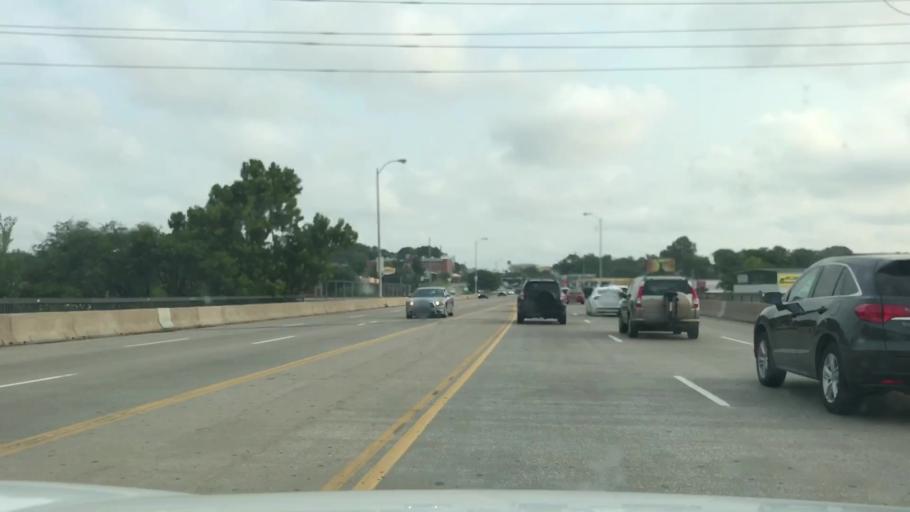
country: US
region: Missouri
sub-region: Saint Louis County
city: Richmond Heights
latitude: 38.6209
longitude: -90.2882
